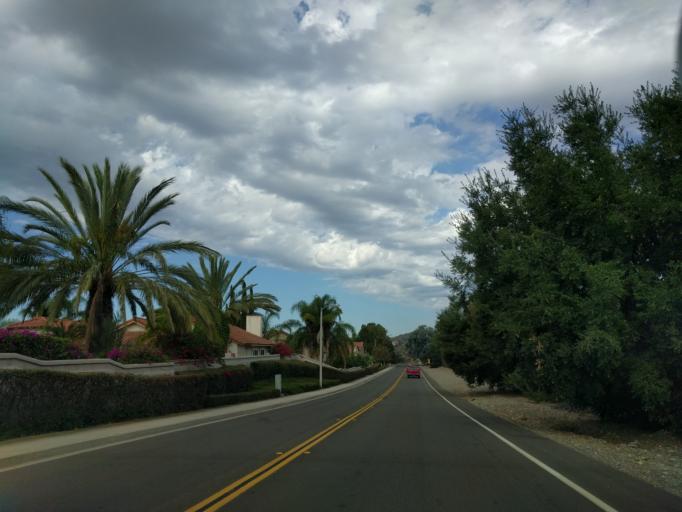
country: US
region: California
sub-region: Orange County
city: Trabuco Canyon
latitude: 33.6575
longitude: -117.5799
